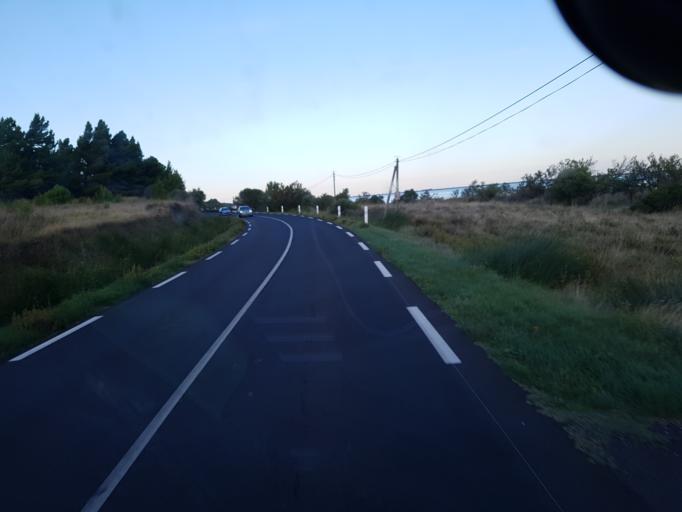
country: FR
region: Languedoc-Roussillon
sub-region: Departement de l'Aude
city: Leucate
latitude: 42.9639
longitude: 2.9952
